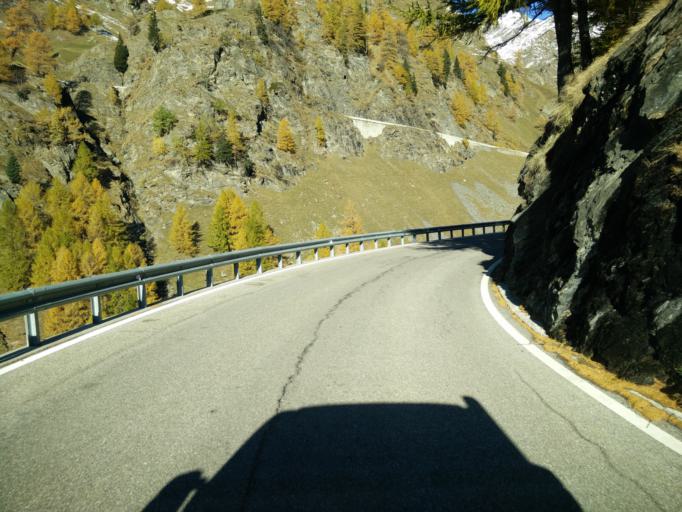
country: IT
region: Trentino-Alto Adige
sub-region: Bolzano
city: Moso in Passiria
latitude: 46.8907
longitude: 11.1311
